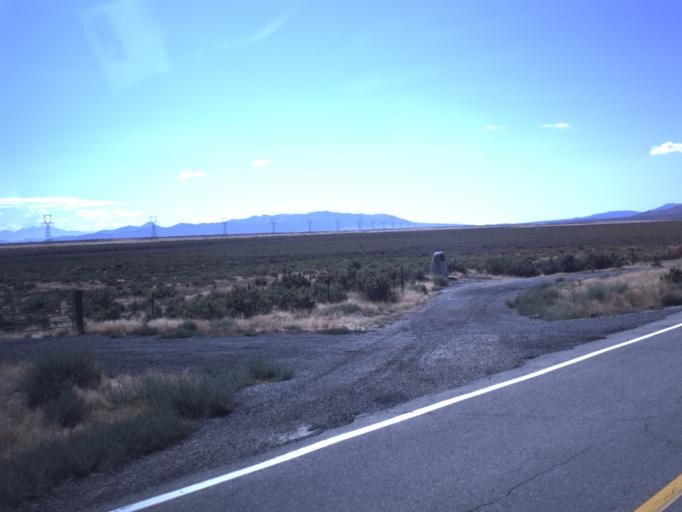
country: US
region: Utah
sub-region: Tooele County
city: Tooele
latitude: 40.2528
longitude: -112.3990
